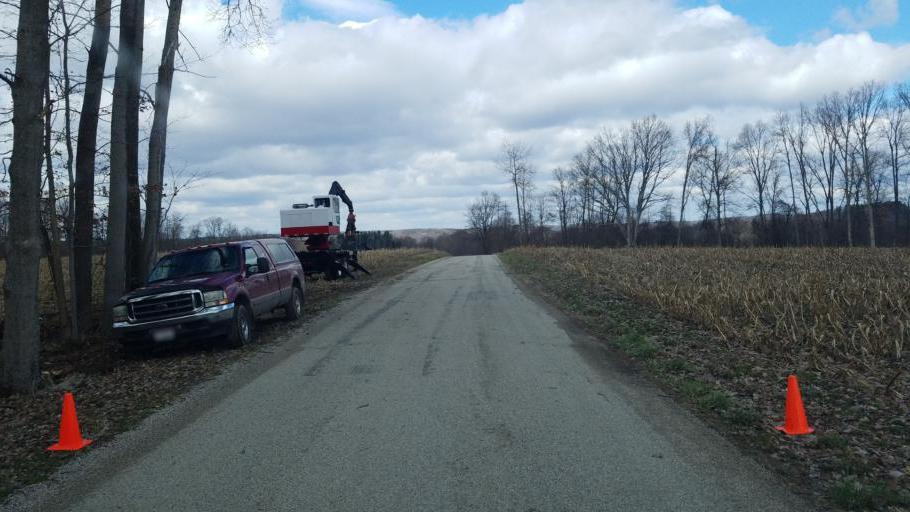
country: US
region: Ohio
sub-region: Sandusky County
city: Bellville
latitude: 40.5860
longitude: -82.4856
